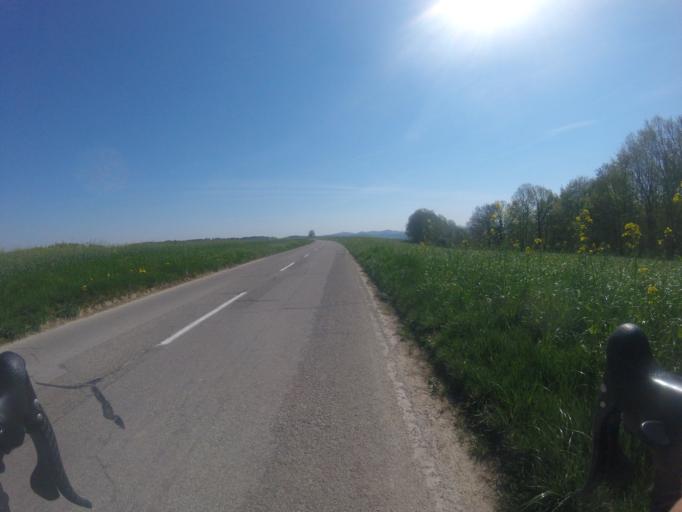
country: CH
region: Bern
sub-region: Bern-Mittelland District
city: Laupen
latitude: 46.9003
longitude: 7.2606
